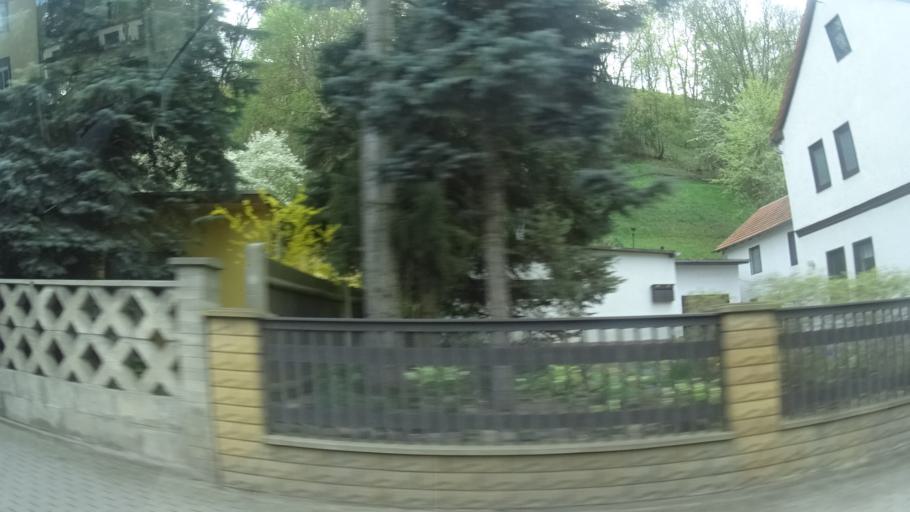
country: DE
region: Thuringia
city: Rudolstadt
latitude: 50.7235
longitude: 11.3404
